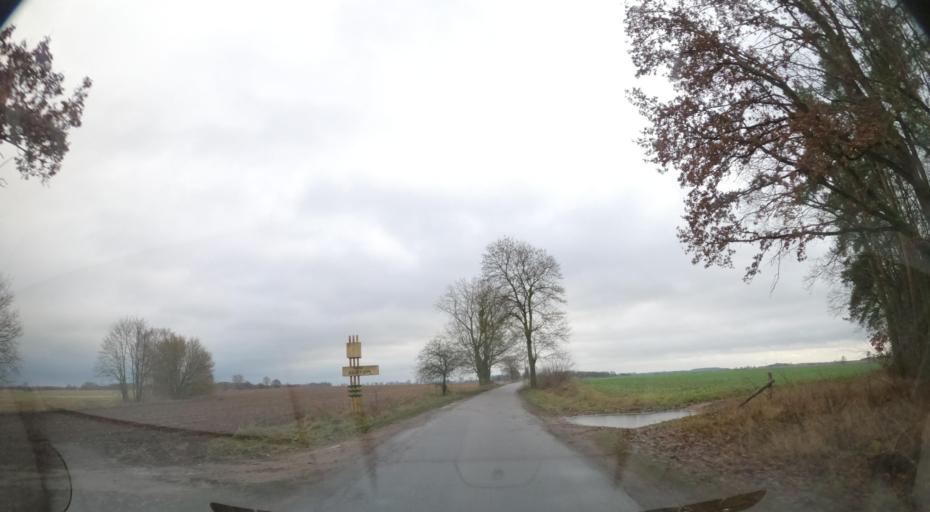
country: PL
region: Greater Poland Voivodeship
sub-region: Powiat zlotowski
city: Zlotow
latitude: 53.2797
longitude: 17.0886
